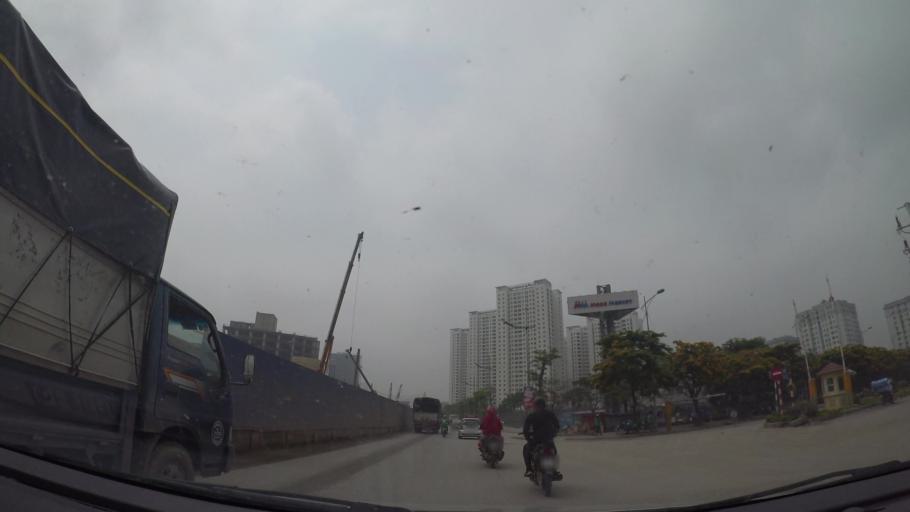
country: VN
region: Ha Noi
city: Cau Dien
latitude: 21.0557
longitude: 105.7820
